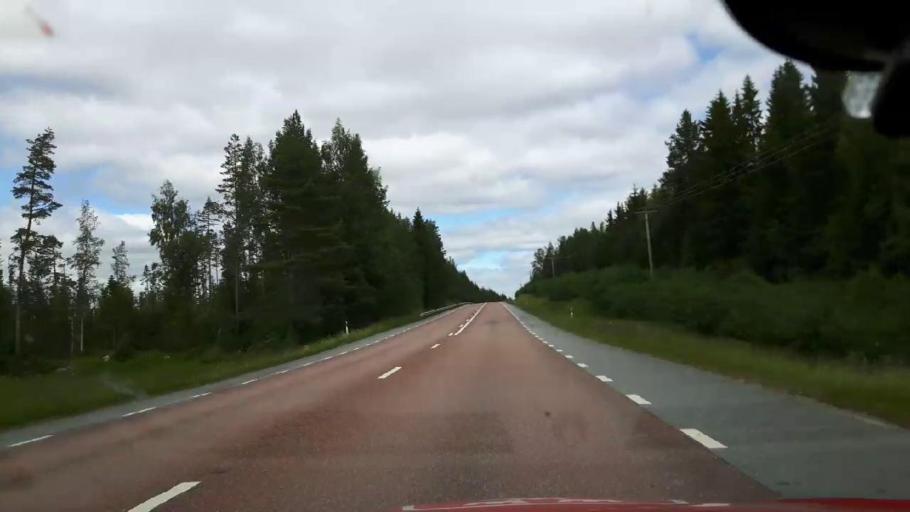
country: SE
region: Jaemtland
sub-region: Braecke Kommun
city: Braecke
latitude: 62.7970
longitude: 15.3732
